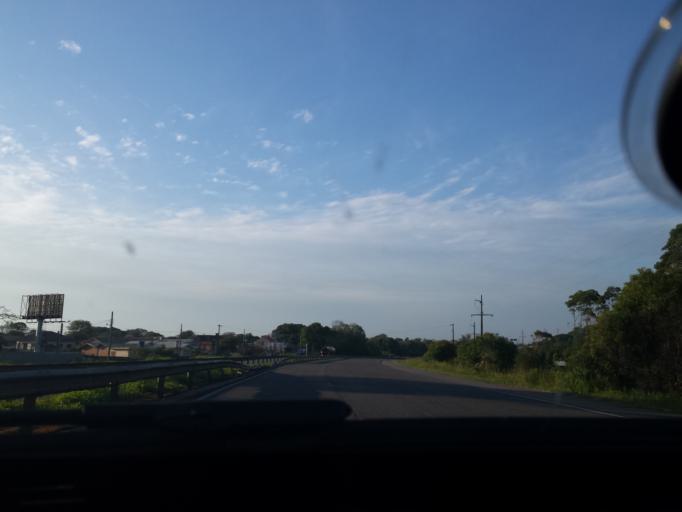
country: BR
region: Santa Catarina
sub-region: Imbituba
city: Imbituba
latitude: -28.2752
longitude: -48.6999
